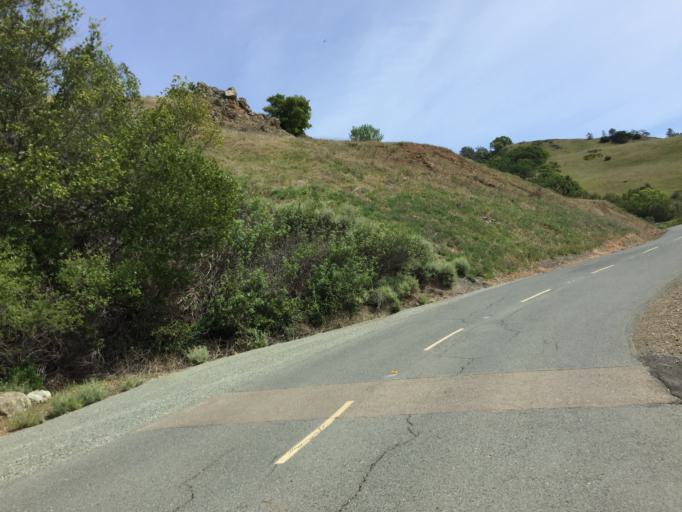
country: US
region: California
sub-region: Contra Costa County
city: Diablo
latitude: 37.8711
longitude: -121.9383
